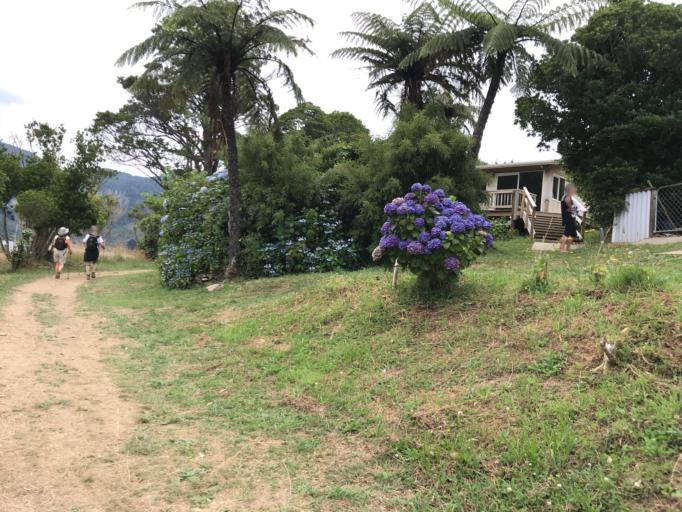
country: NZ
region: Marlborough
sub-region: Marlborough District
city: Picton
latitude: -41.1019
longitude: 174.1843
